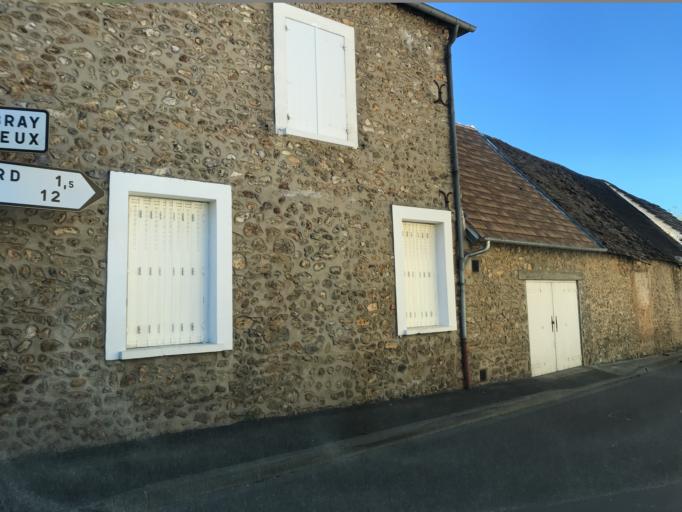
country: FR
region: Haute-Normandie
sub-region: Departement de l'Eure
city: Houlbec-Cocherel
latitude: 49.0950
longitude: 1.3383
